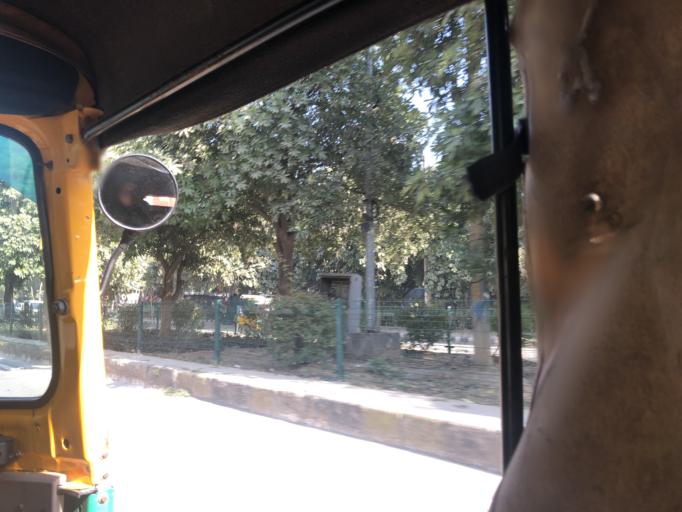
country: IN
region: Haryana
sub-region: Gurgaon
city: Gurgaon
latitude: 28.4331
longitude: 77.0908
